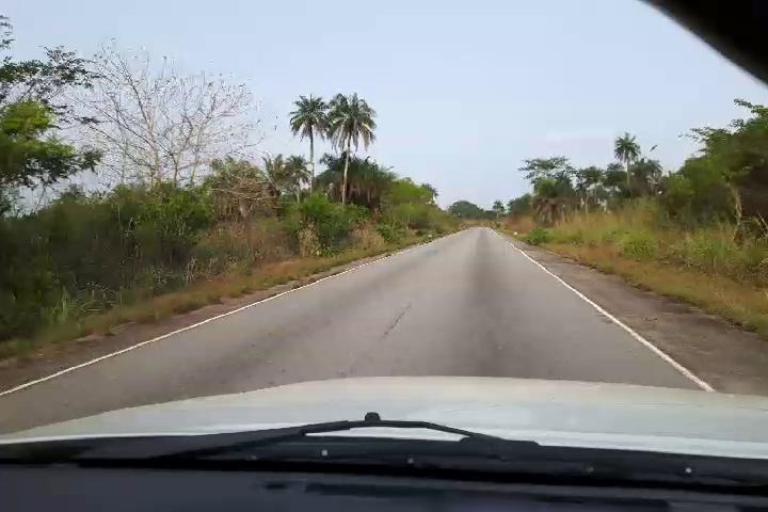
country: SL
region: Southern Province
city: Baoma
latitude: 7.9248
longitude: -11.5362
